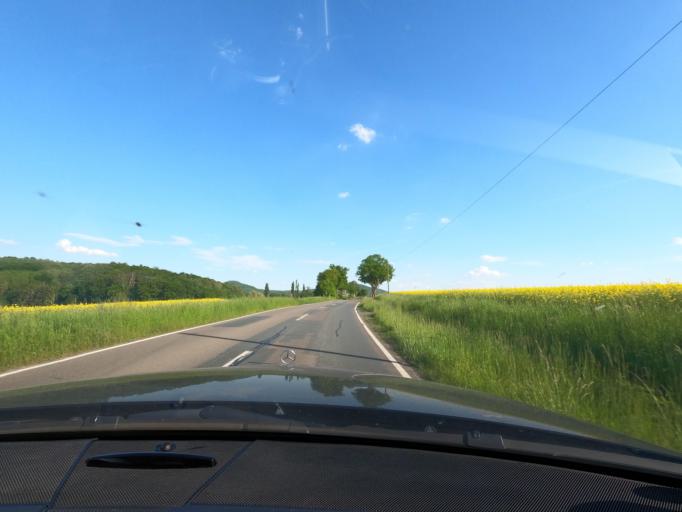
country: DE
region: Hesse
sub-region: Regierungsbezirk Kassel
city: Martinhagen
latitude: 51.3280
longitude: 9.2502
